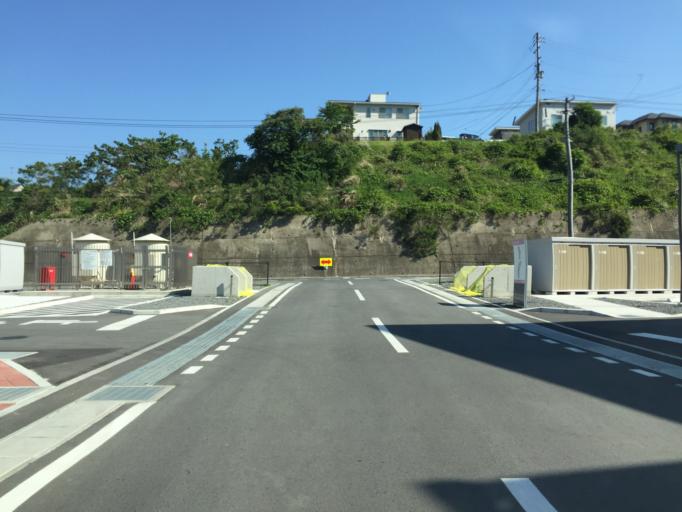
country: JP
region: Fukushima
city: Iwaki
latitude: 36.9667
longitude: 140.8656
